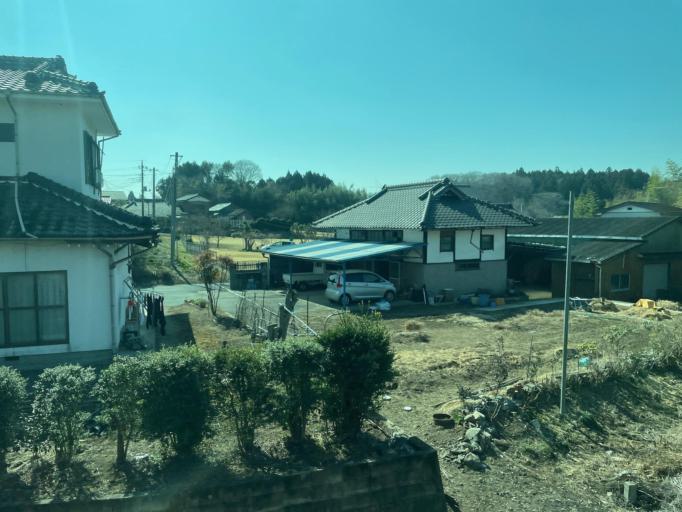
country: JP
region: Ibaraki
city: Omiya
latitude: 36.6058
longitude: 140.3898
